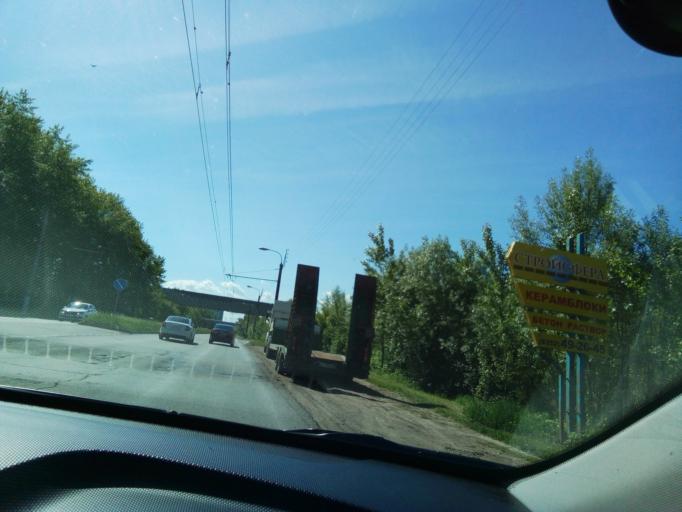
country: RU
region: Chuvashia
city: Novocheboksarsk
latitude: 56.0841
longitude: 47.5035
